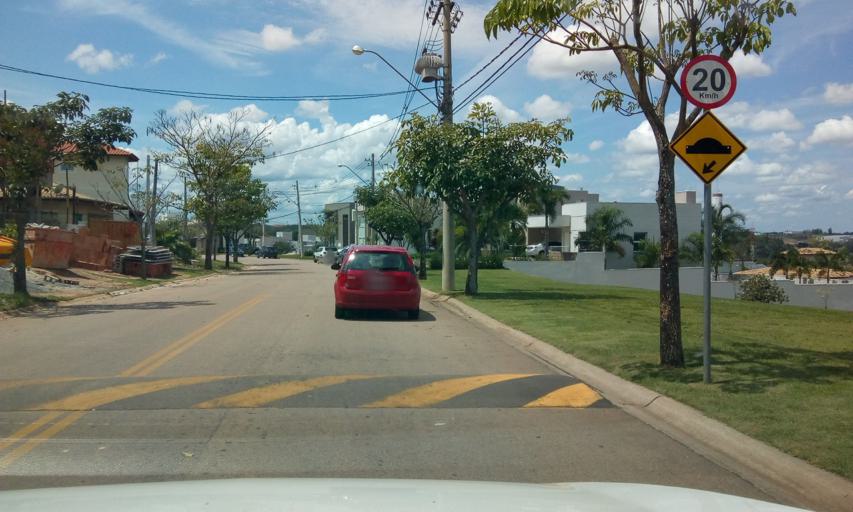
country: BR
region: Sao Paulo
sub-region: Itupeva
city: Itupeva
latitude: -23.1408
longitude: -47.0507
